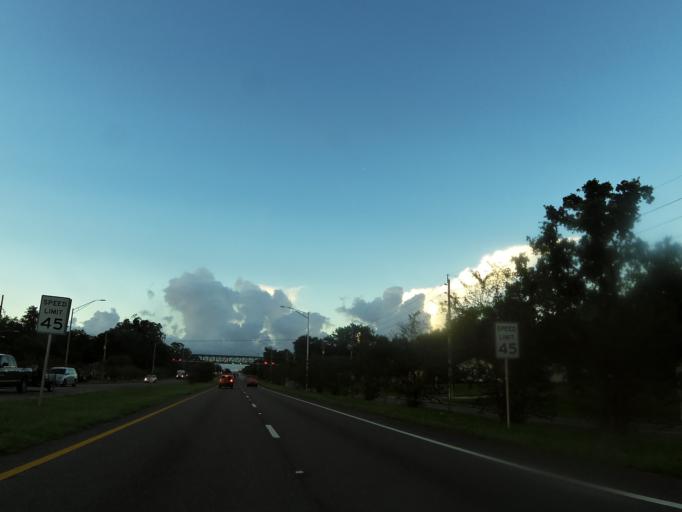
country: US
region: Florida
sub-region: Duval County
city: Jacksonville
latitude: 30.2976
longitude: -81.5585
